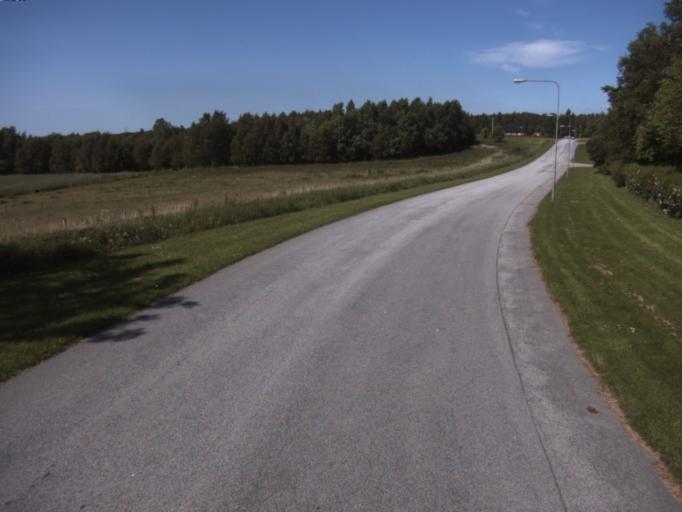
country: SE
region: Skane
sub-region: Helsingborg
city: Gantofta
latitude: 55.9897
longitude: 12.7962
